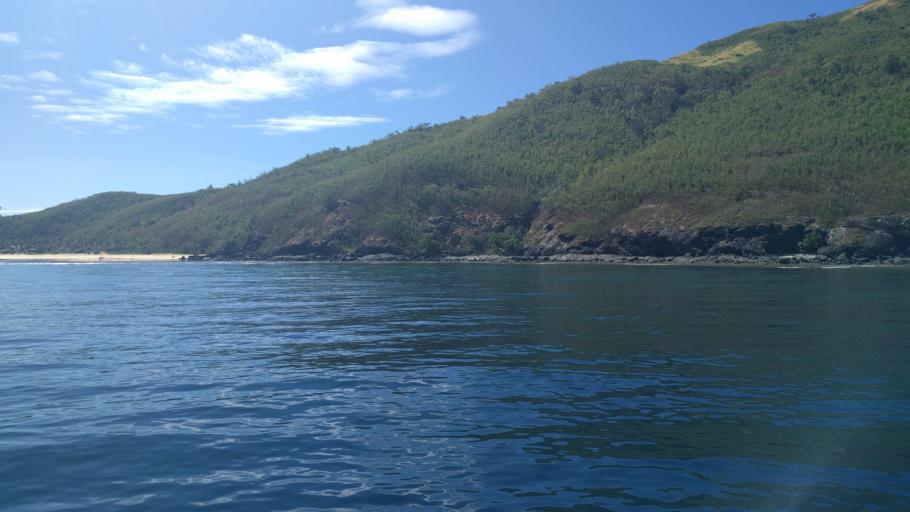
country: FJ
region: Western
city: Lautoka
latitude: -17.2823
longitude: 177.1032
